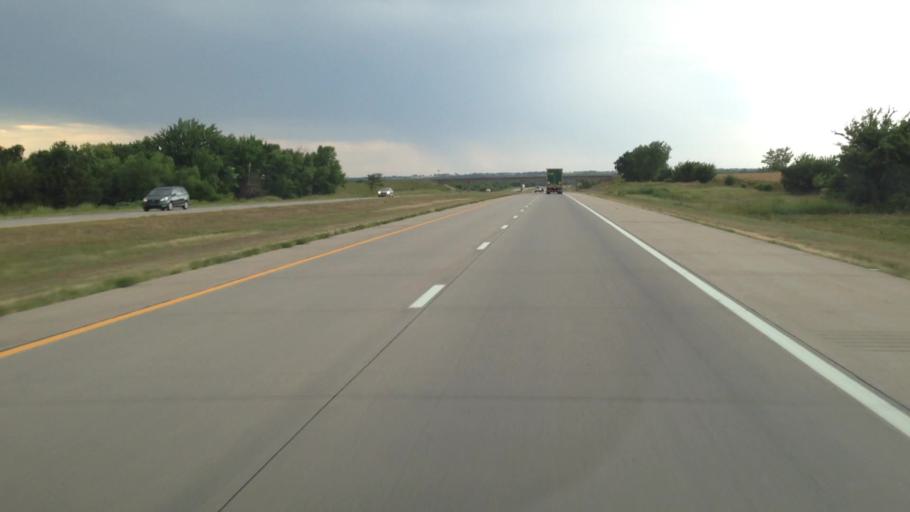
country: US
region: Kansas
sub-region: Osage County
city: Lyndon
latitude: 38.4571
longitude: -95.5589
